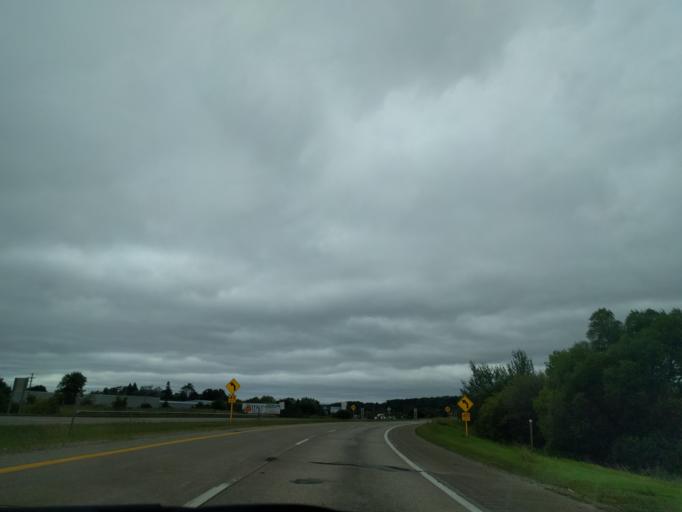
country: US
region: Michigan
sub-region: Delta County
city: Gladstone
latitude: 45.8506
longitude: -87.0244
